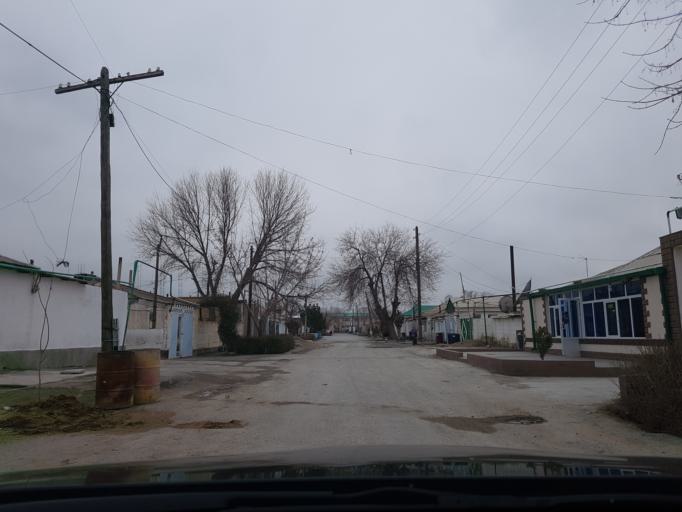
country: TM
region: Ahal
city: Abadan
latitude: 38.1545
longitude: 57.9647
